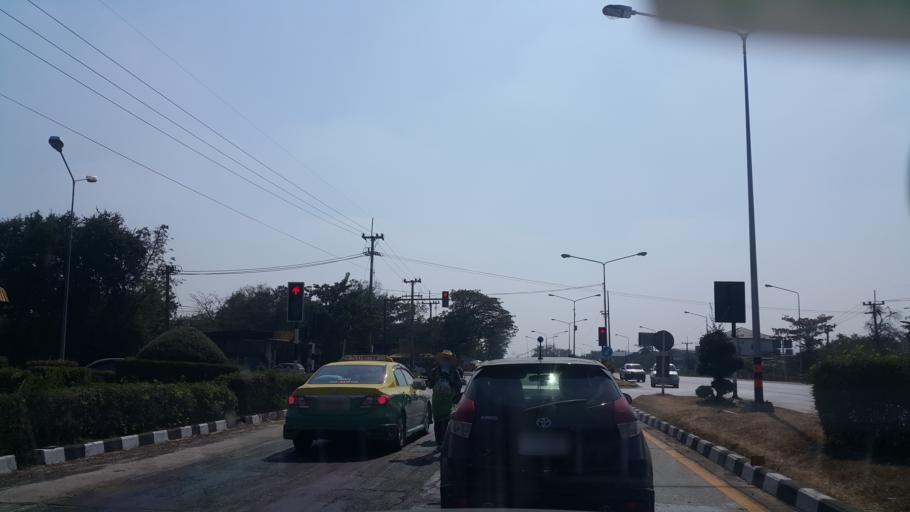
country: TH
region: Nakhon Ratchasima
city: Non Daeng
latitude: 15.3486
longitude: 102.4460
